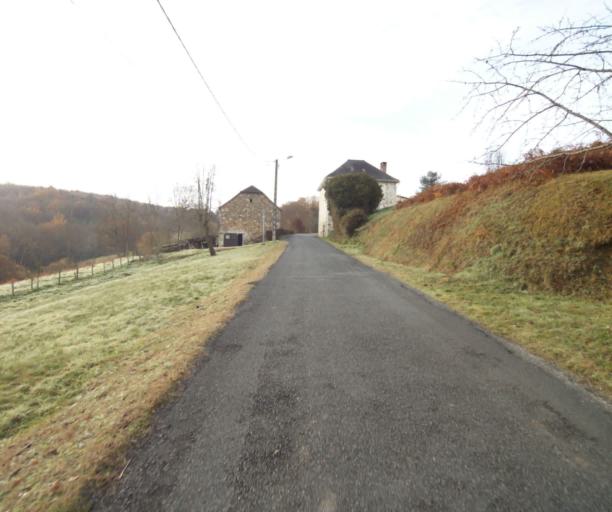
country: FR
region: Limousin
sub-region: Departement de la Correze
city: Chameyrat
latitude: 45.2202
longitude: 1.7180
